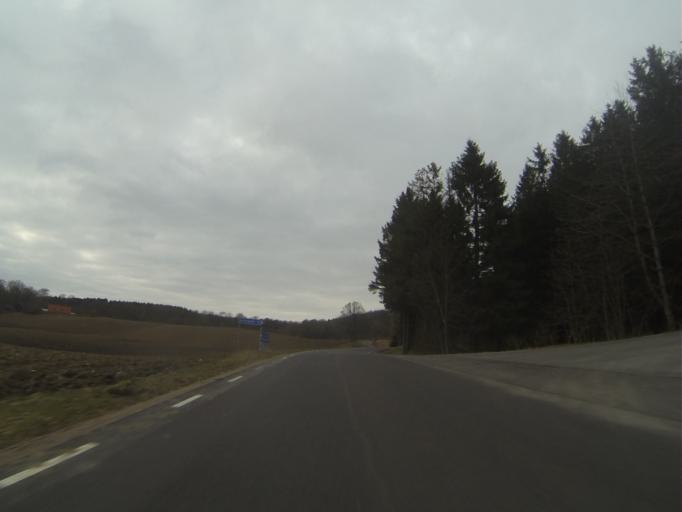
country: SE
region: Skane
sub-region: Lunds Kommun
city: Genarp
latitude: 55.5504
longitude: 13.4420
